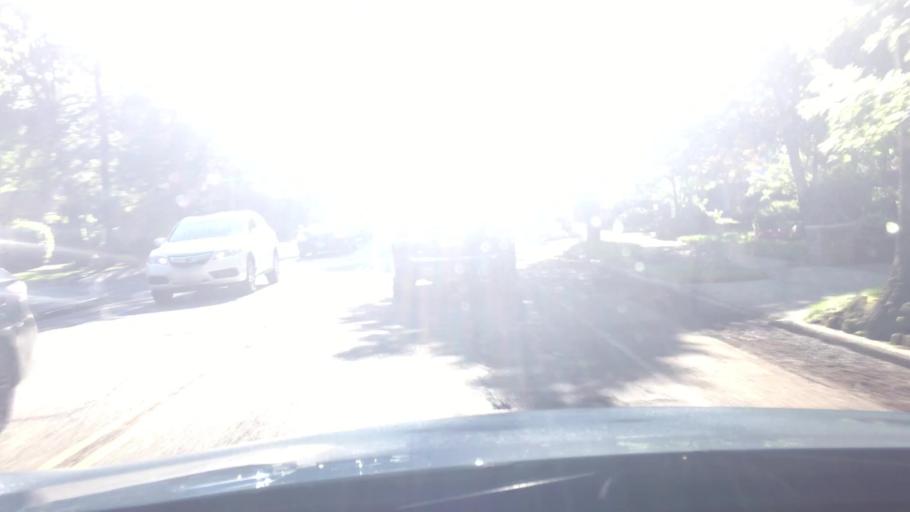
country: US
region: New York
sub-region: Nassau County
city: Albertson
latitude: 40.7717
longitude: -73.6359
